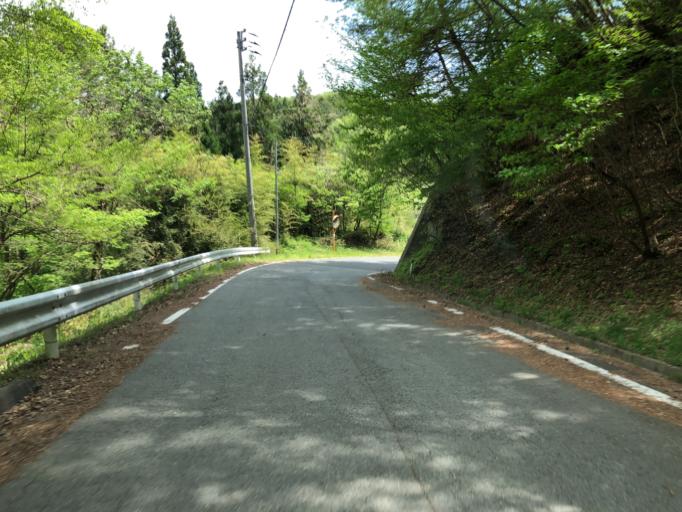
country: JP
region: Miyagi
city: Marumori
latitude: 37.6970
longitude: 140.7785
